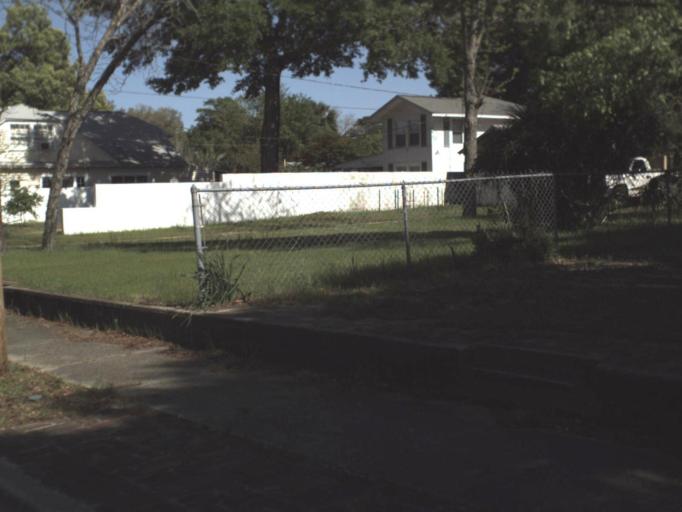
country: US
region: Florida
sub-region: Escambia County
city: East Pensacola Heights
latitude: 30.4254
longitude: -87.1934
